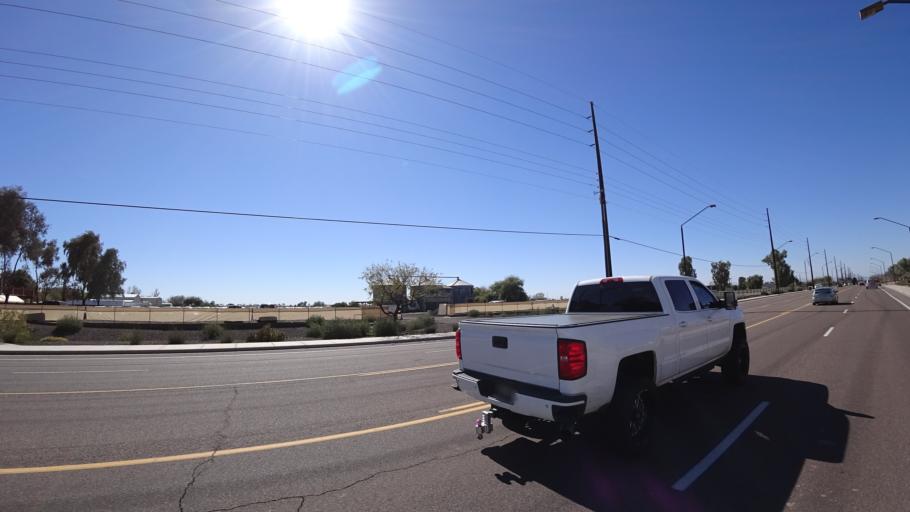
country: US
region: Arizona
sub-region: Maricopa County
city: Gilbert
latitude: 33.2922
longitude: -111.7665
